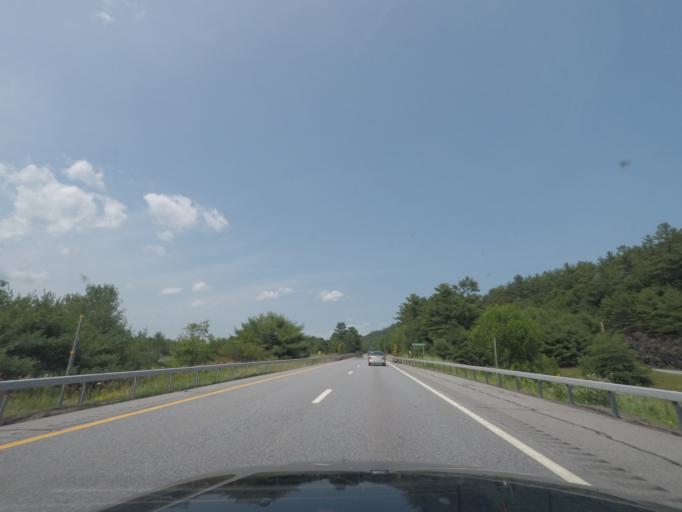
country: US
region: New York
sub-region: Warren County
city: Warrensburg
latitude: 43.4989
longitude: -73.7473
